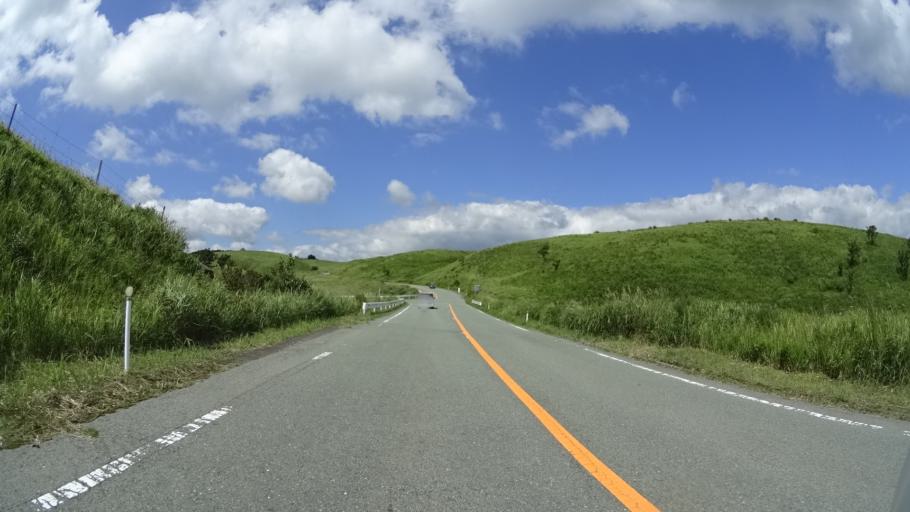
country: JP
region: Kumamoto
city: Aso
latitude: 33.0034
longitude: 131.1306
